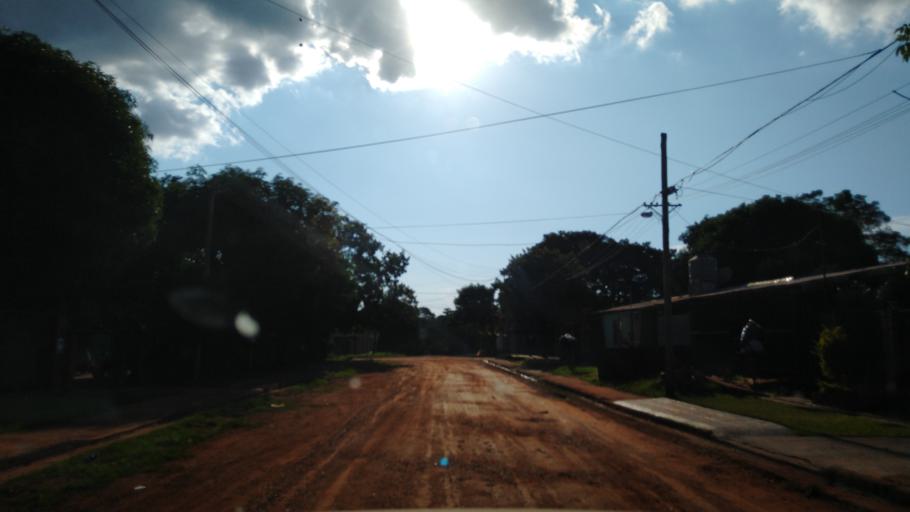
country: AR
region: Misiones
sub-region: Departamento de Capital
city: Posadas
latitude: -27.4058
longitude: -55.9300
